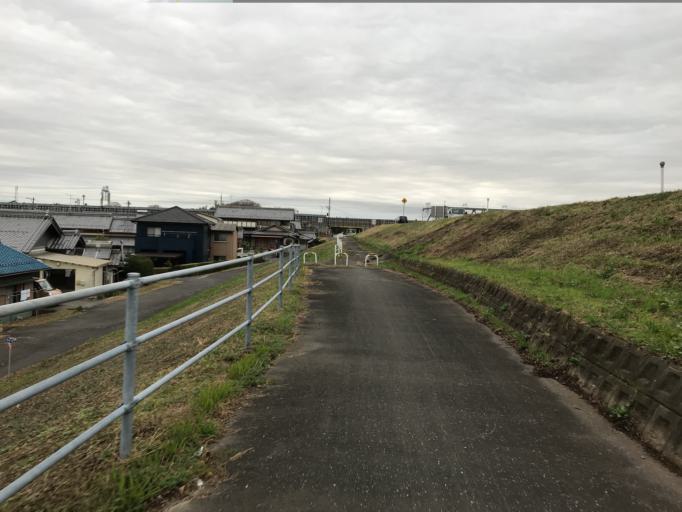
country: JP
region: Gifu
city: Ogaki
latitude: 35.3248
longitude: 136.6716
